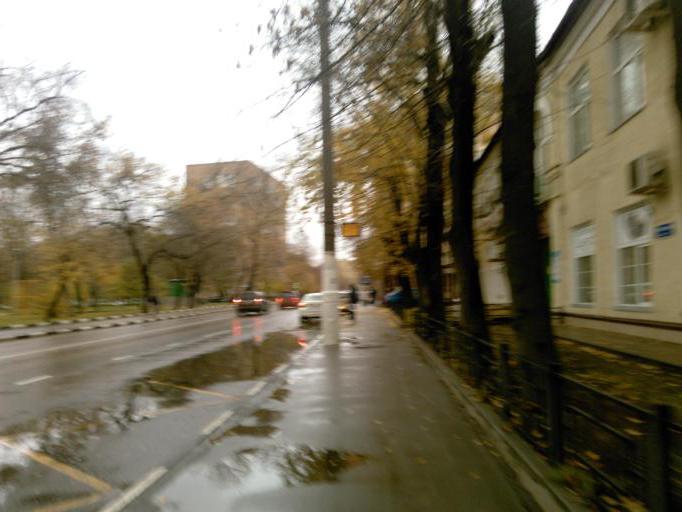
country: RU
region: Moscow
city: Zamoskvorech'ye
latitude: 55.7072
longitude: 37.6181
